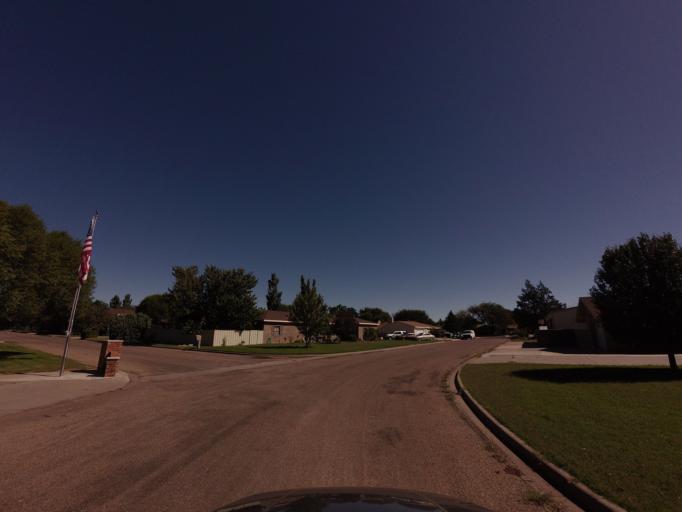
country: US
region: New Mexico
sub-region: Curry County
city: Clovis
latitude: 34.4240
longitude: -103.1884
